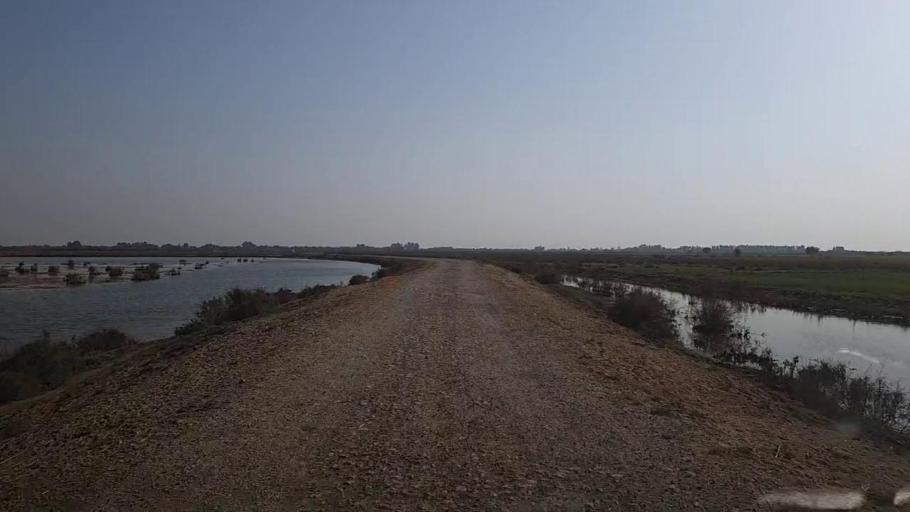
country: PK
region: Sindh
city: Kandhkot
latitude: 28.3659
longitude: 69.3297
